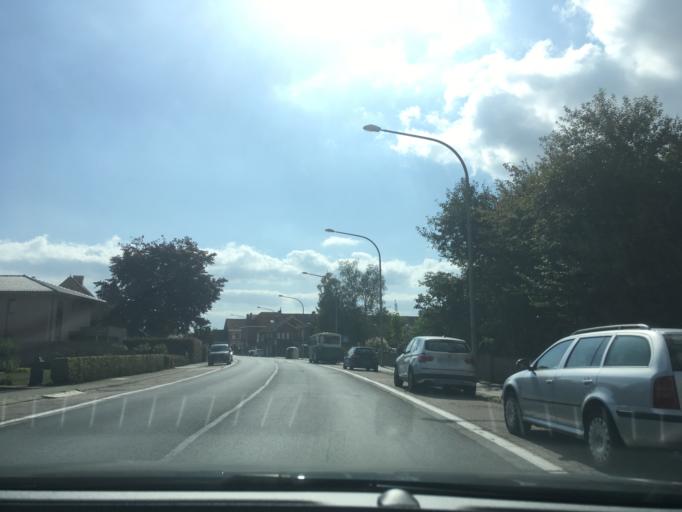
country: BE
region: Flanders
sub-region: Provincie West-Vlaanderen
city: Ieper
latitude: 50.8567
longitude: 2.8981
